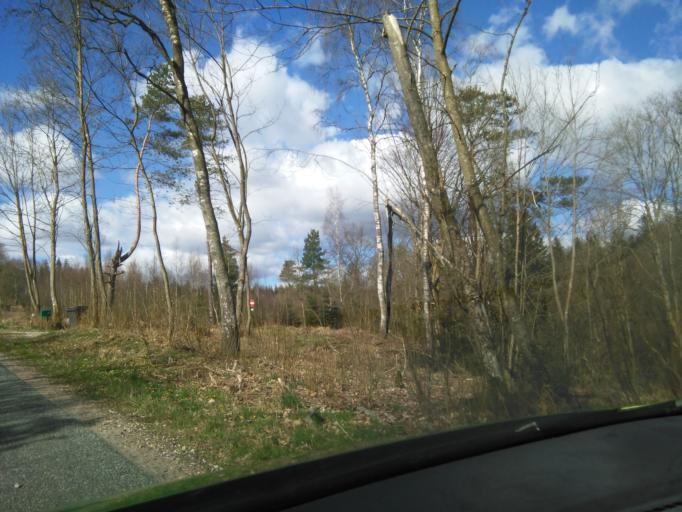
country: DK
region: Central Jutland
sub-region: Silkeborg Kommune
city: Virklund
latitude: 56.0406
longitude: 9.4814
